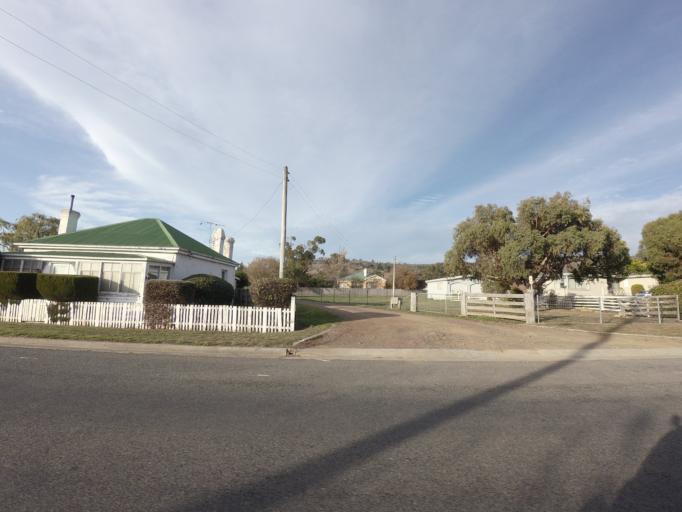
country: AU
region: Tasmania
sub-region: Brighton
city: Bridgewater
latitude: -42.5394
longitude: 147.2044
